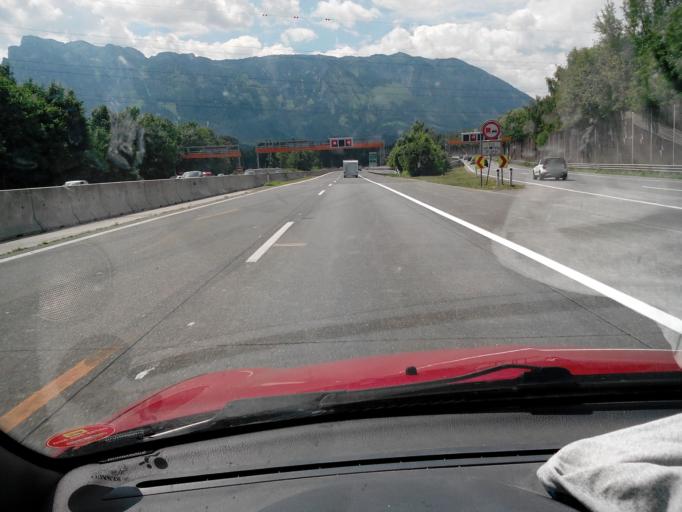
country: DE
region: Bavaria
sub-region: Upper Bavaria
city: Ainring
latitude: 47.7796
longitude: 12.9802
